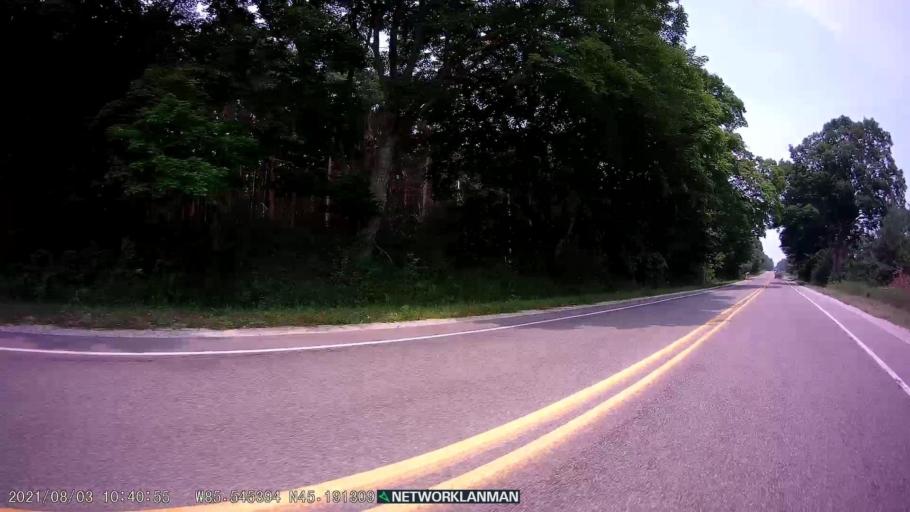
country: US
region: Michigan
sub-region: Leelanau County
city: Leland
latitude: 45.1917
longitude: -85.5454
